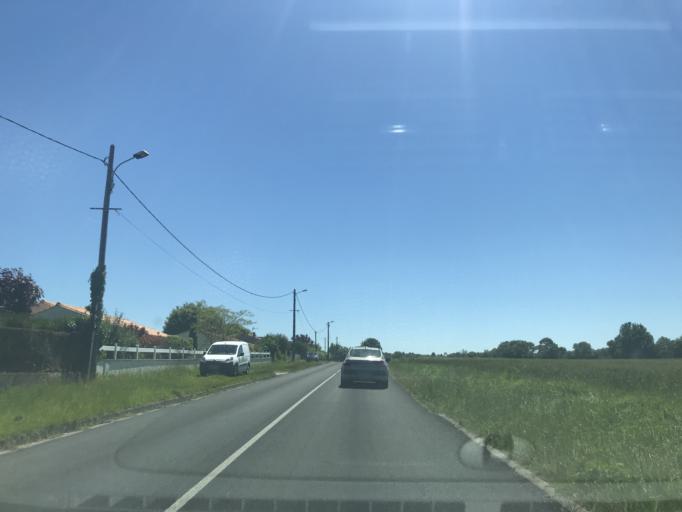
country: FR
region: Poitou-Charentes
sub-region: Departement de la Charente-Maritime
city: Meschers-sur-Gironde
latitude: 45.5857
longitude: -0.9599
